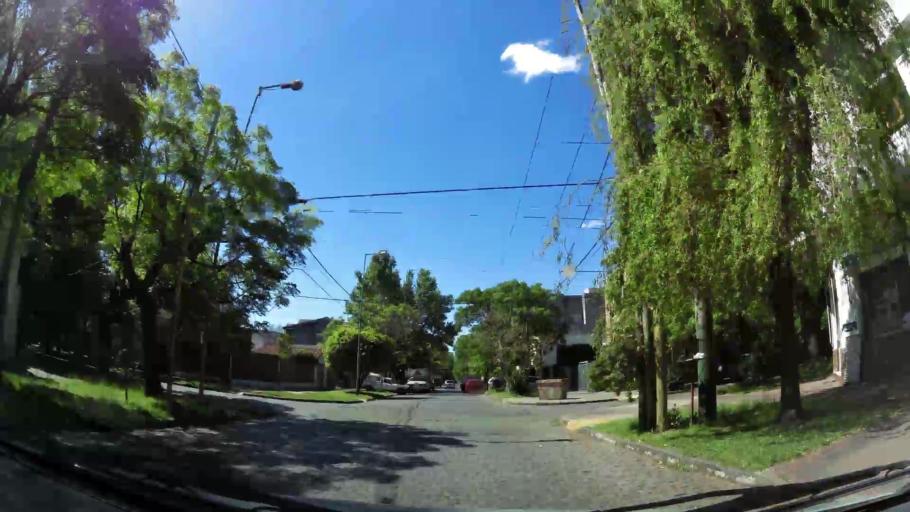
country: AR
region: Buenos Aires
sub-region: Partido de Lomas de Zamora
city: Lomas de Zamora
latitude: -34.7382
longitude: -58.4039
